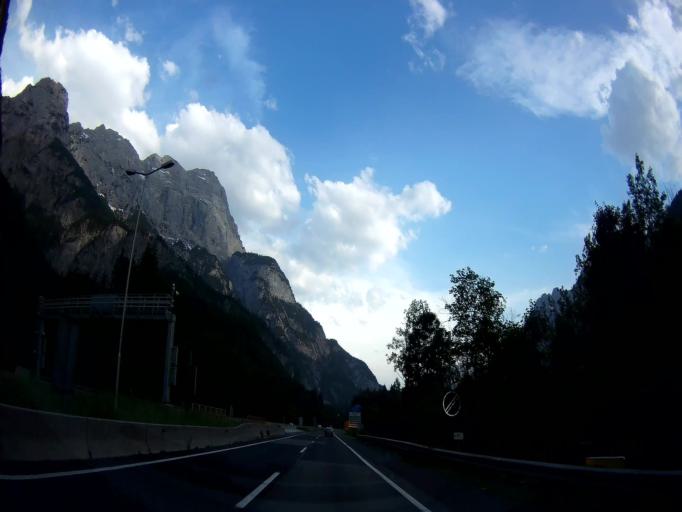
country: AT
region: Salzburg
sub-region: Politischer Bezirk Hallein
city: Golling an der Salzach
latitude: 47.5541
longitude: 13.1747
